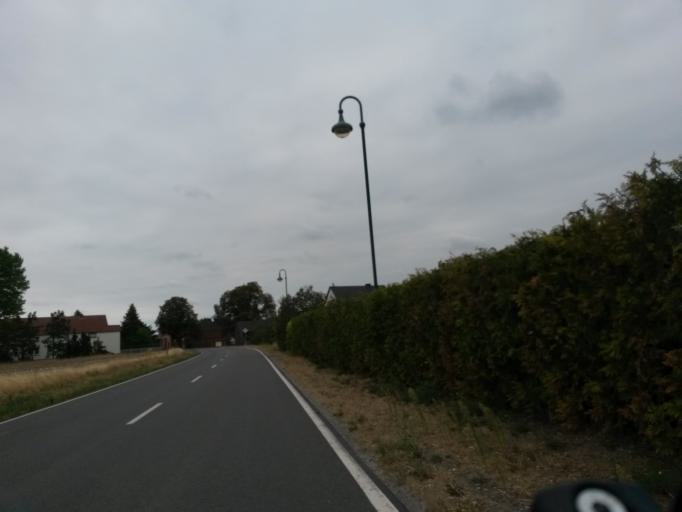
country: DE
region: Saxony-Anhalt
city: Muhlanger
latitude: 51.8688
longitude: 12.7848
